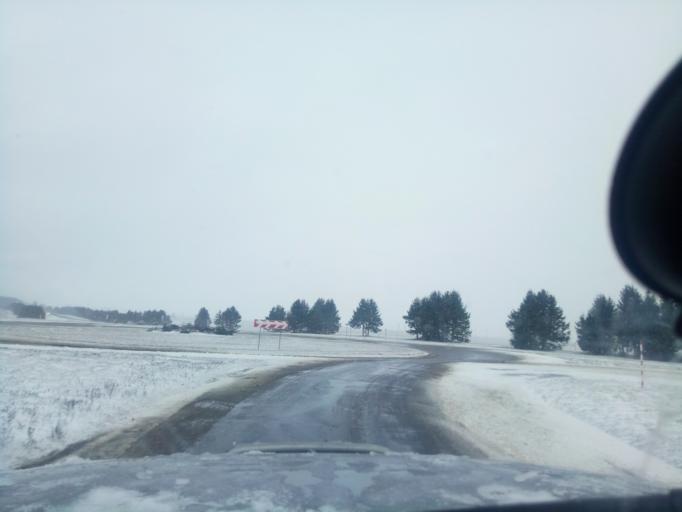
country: BY
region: Minsk
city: Haradzyeya
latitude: 53.2945
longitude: 26.5751
